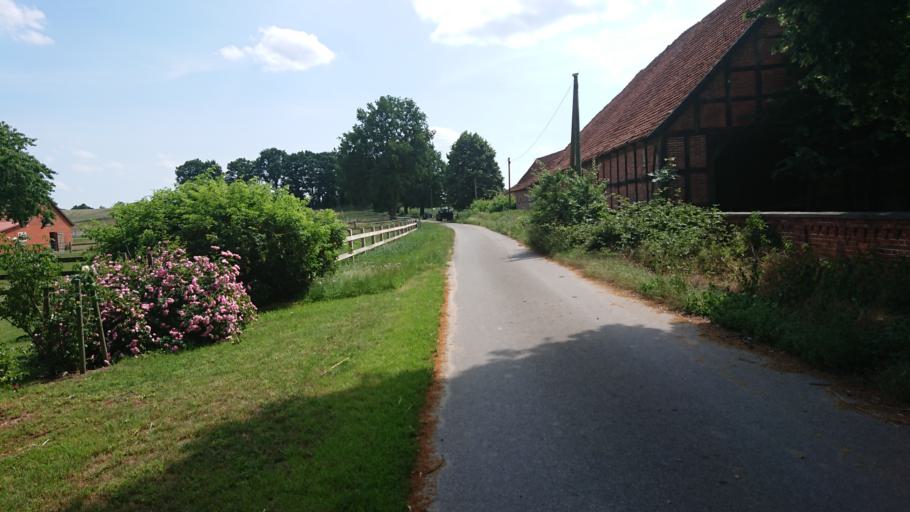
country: DE
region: Lower Saxony
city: Husum
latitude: 52.5455
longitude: 9.2105
